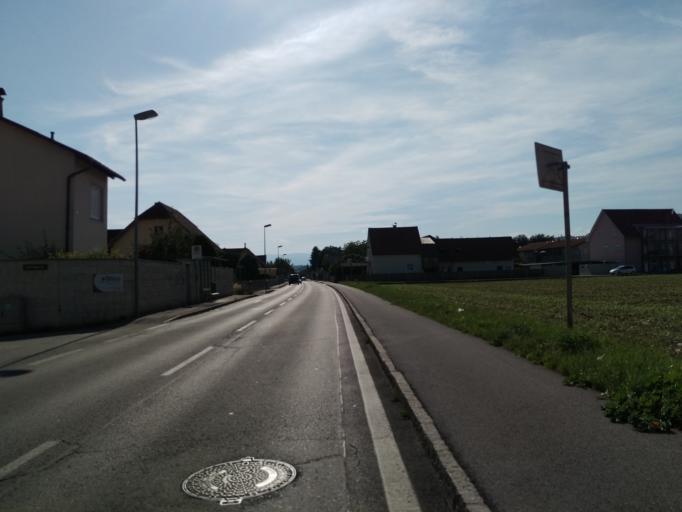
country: AT
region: Styria
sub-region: Politischer Bezirk Graz-Umgebung
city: Seiersberg
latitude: 47.0140
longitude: 15.4231
